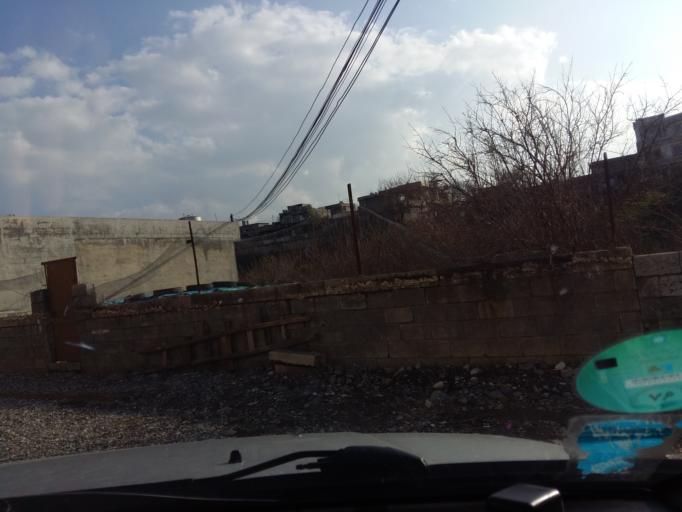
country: IQ
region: As Sulaymaniyah
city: Qeladize
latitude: 36.1753
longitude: 45.1376
